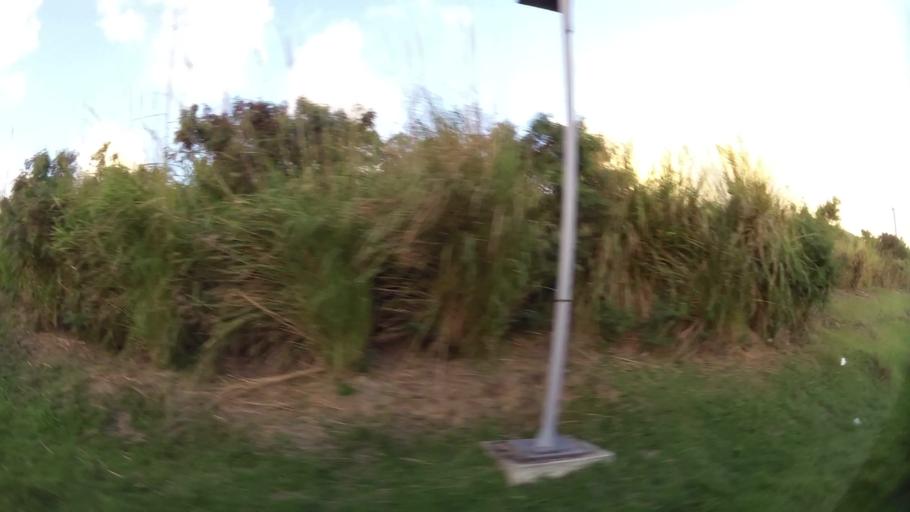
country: KN
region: Saint Anne Sandy Point
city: Sandy Point Town
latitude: 17.3761
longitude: -62.8538
